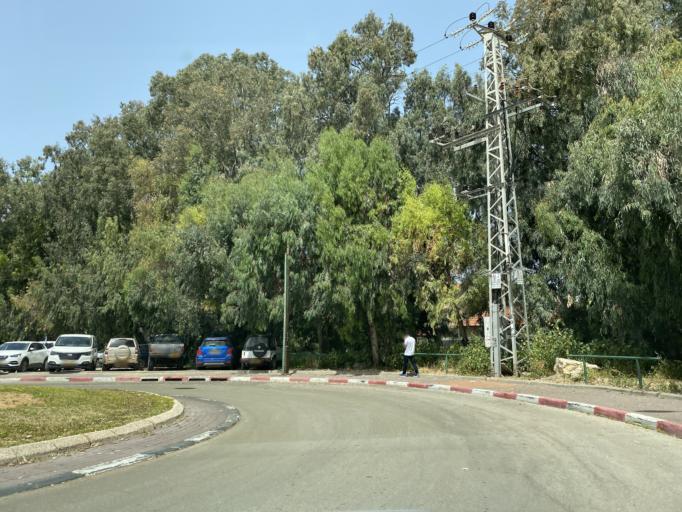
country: IL
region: Tel Aviv
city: Herzliya Pituah
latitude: 32.1678
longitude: 34.8120
